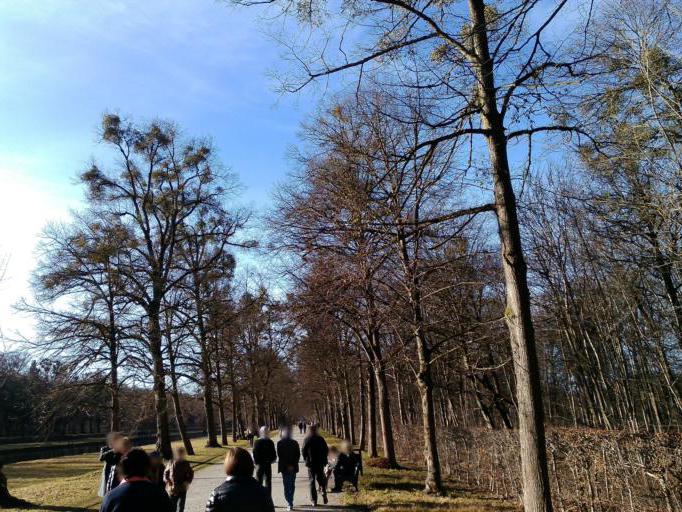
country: DE
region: Bavaria
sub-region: Upper Bavaria
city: Pasing
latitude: 48.1582
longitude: 11.4949
